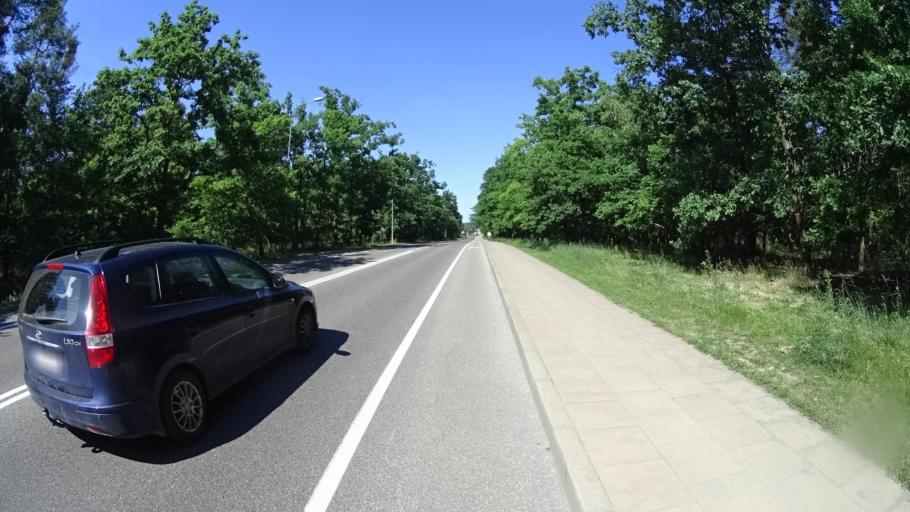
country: PL
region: Masovian Voivodeship
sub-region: Warszawa
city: Bialoleka
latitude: 52.3487
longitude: 20.9576
